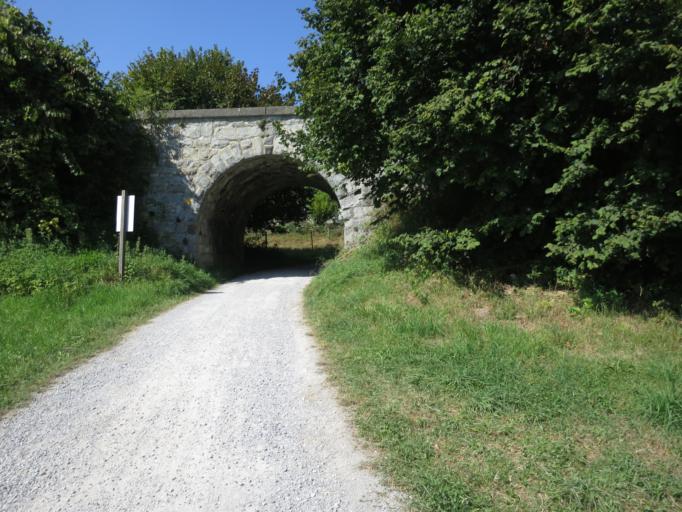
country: CH
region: Zurich
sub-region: Bezirk Hinwil
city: Bubikon
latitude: 47.2623
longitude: 8.8183
